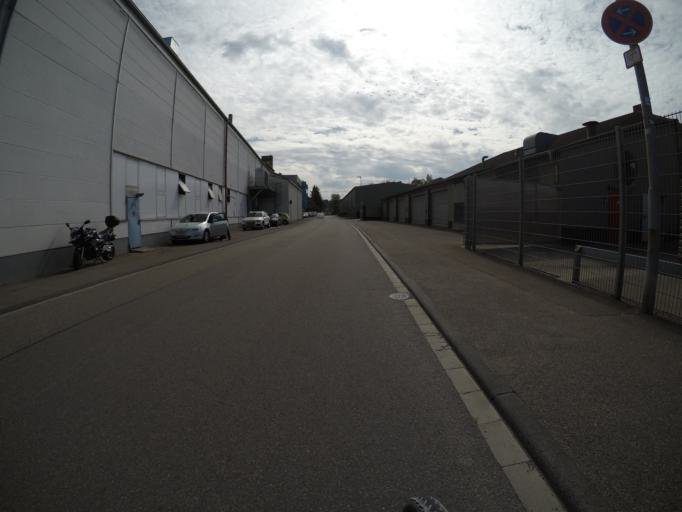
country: DE
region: Baden-Wuerttemberg
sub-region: Karlsruhe Region
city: Zaisenhausen
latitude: 49.1101
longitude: 8.7409
